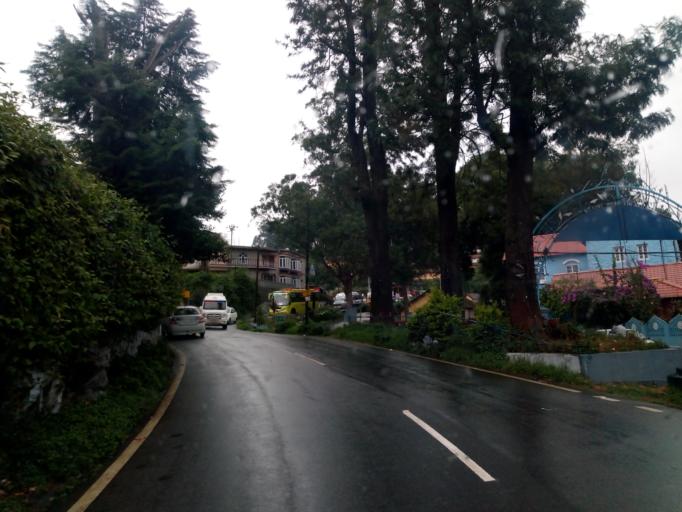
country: IN
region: Tamil Nadu
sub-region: Nilgiri
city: Wellington
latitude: 11.3438
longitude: 76.7919
